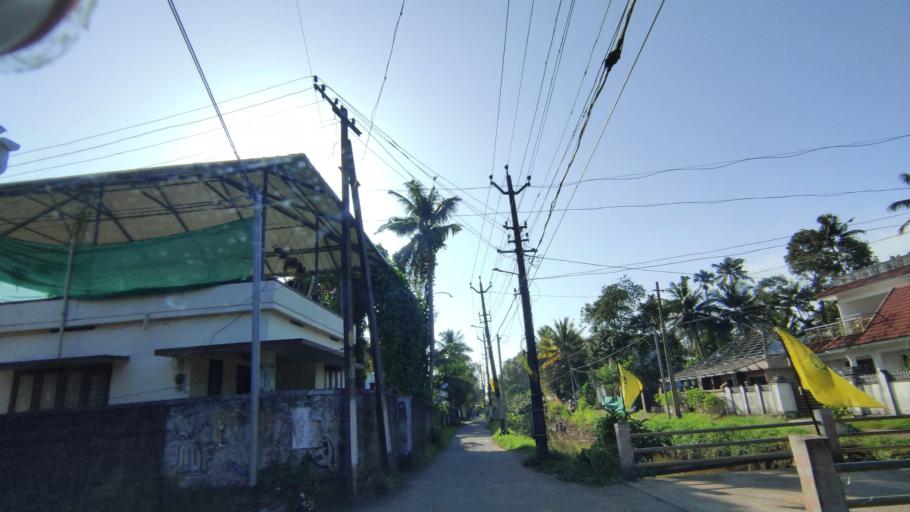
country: IN
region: Kerala
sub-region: Kottayam
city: Kottayam
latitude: 9.5928
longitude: 76.5053
